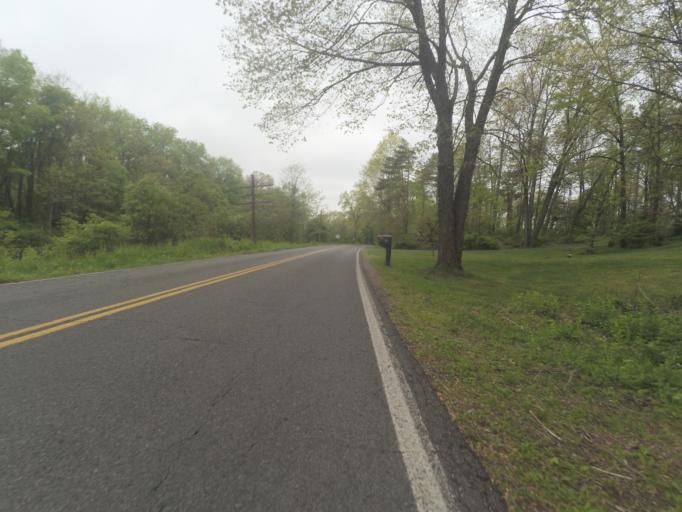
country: US
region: Ohio
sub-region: Portage County
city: Kent
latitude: 41.1729
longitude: -81.3142
